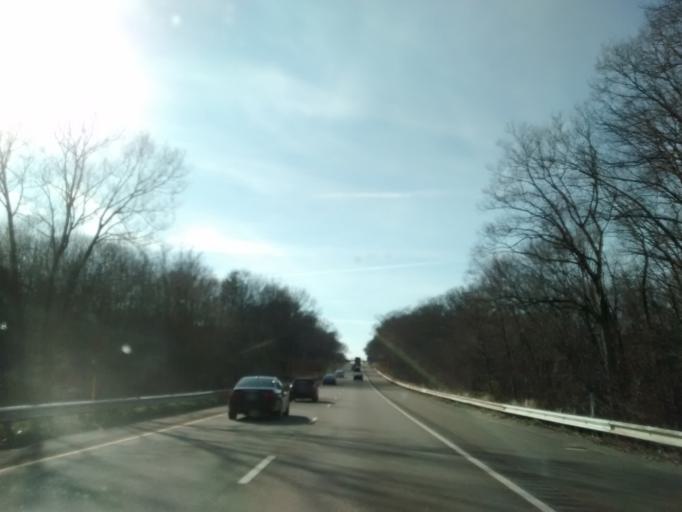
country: US
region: Massachusetts
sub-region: Worcester County
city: Uxbridge
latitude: 42.0580
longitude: -71.6432
